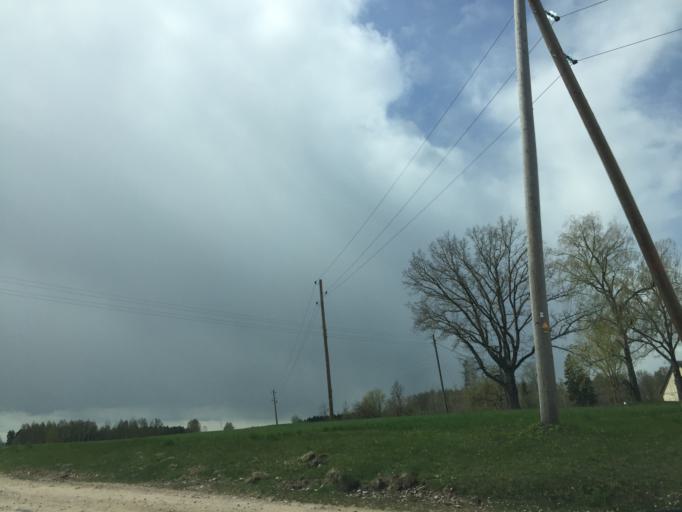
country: LV
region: Lecava
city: Iecava
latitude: 56.6580
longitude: 24.2160
